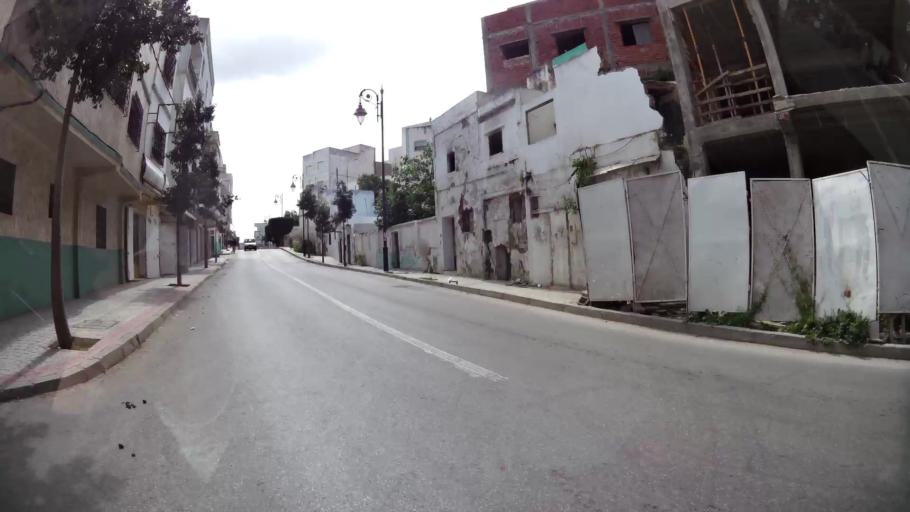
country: MA
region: Tanger-Tetouan
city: Tetouan
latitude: 35.5817
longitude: -5.3598
